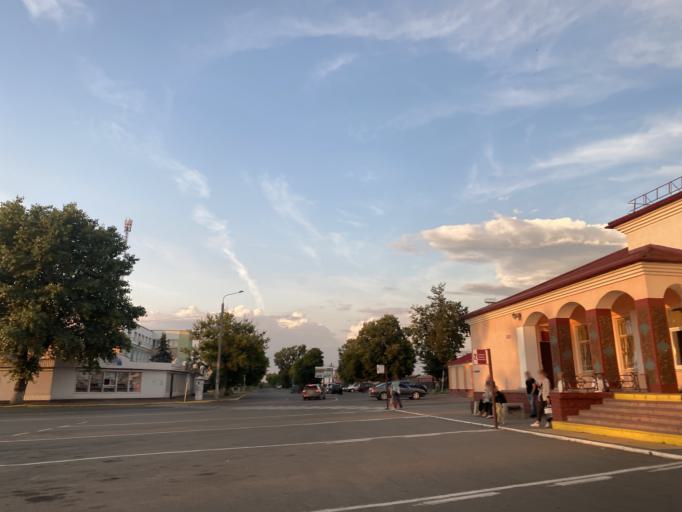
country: BY
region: Brest
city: Ivatsevichy
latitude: 52.7094
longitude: 25.3444
